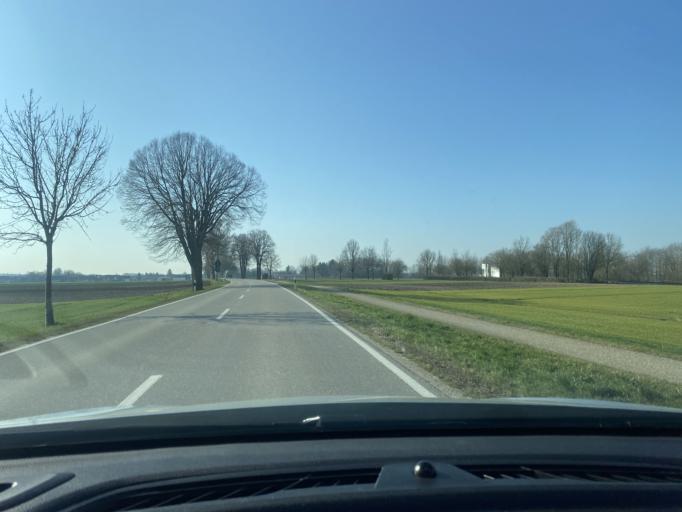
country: DE
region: Bavaria
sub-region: Upper Bavaria
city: Oberding
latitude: 48.3148
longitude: 11.8480
